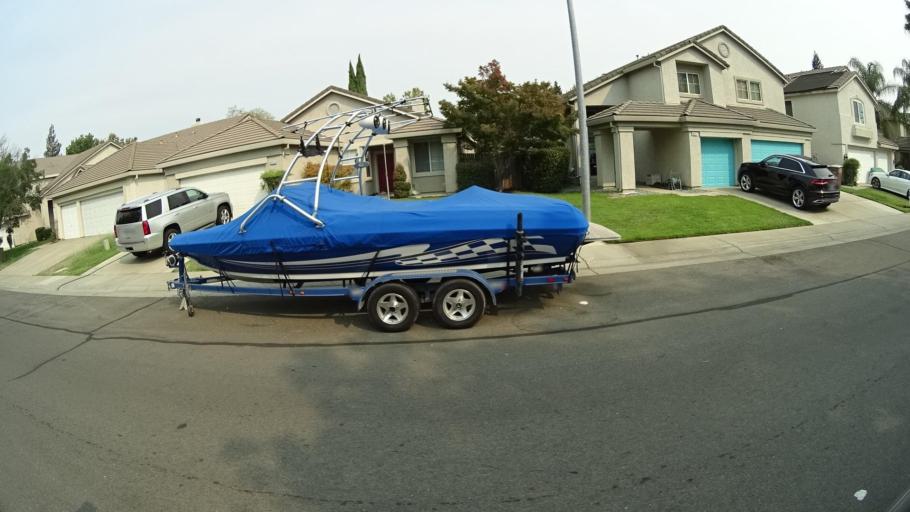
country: US
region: California
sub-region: Sacramento County
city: Laguna
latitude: 38.4127
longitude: -121.4032
